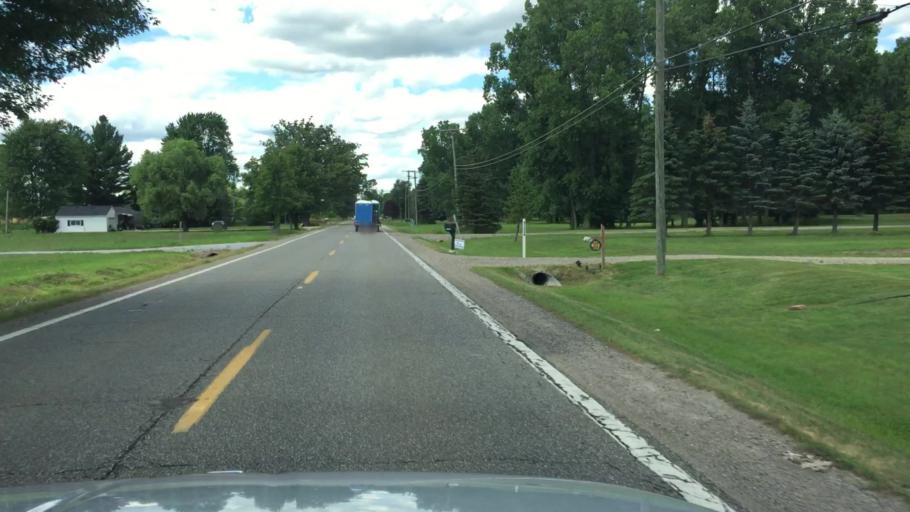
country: US
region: Michigan
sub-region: Macomb County
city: Armada
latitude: 42.8691
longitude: -82.9450
